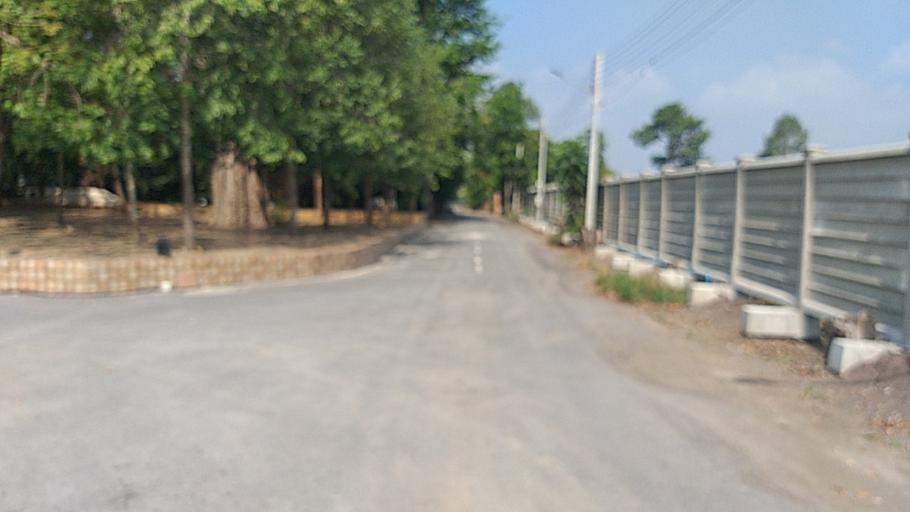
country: TH
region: Pathum Thani
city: Nong Suea
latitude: 14.1885
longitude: 100.8357
